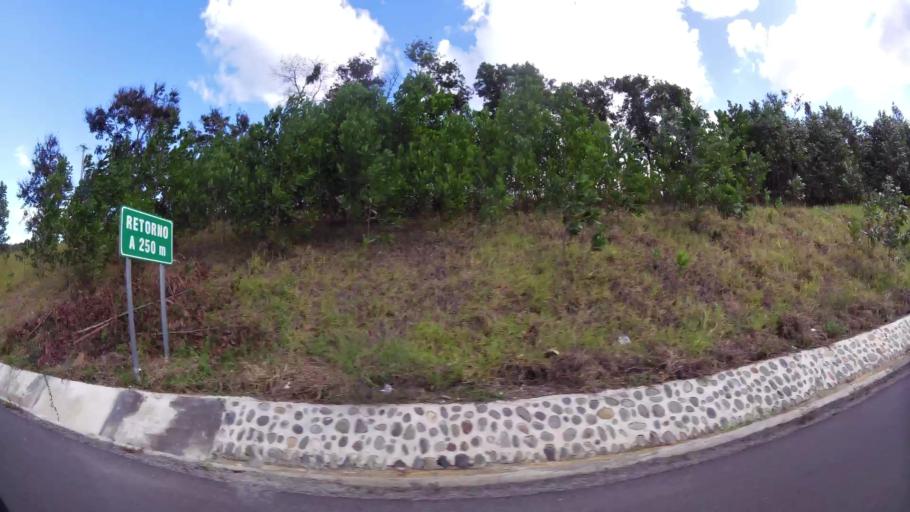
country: DO
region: Santo Domingo
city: Santo Domingo Oeste
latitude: 18.5494
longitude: -70.0773
